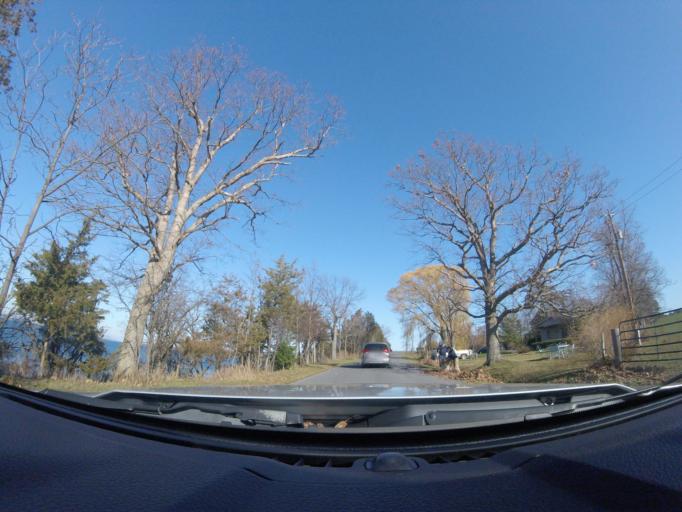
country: US
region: New York
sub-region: Cayuga County
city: Union Springs
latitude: 42.7318
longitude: -76.7086
